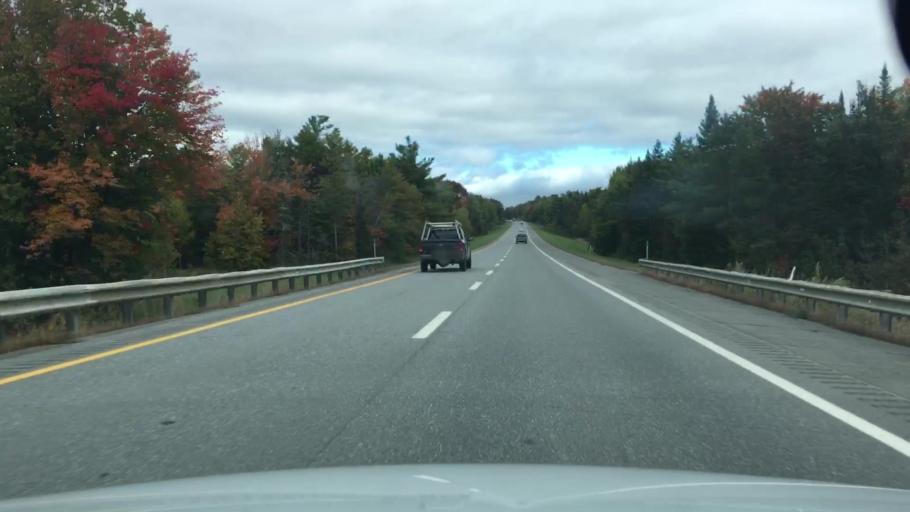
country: US
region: Maine
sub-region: Penobscot County
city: Carmel
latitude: 44.7755
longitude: -69.0438
